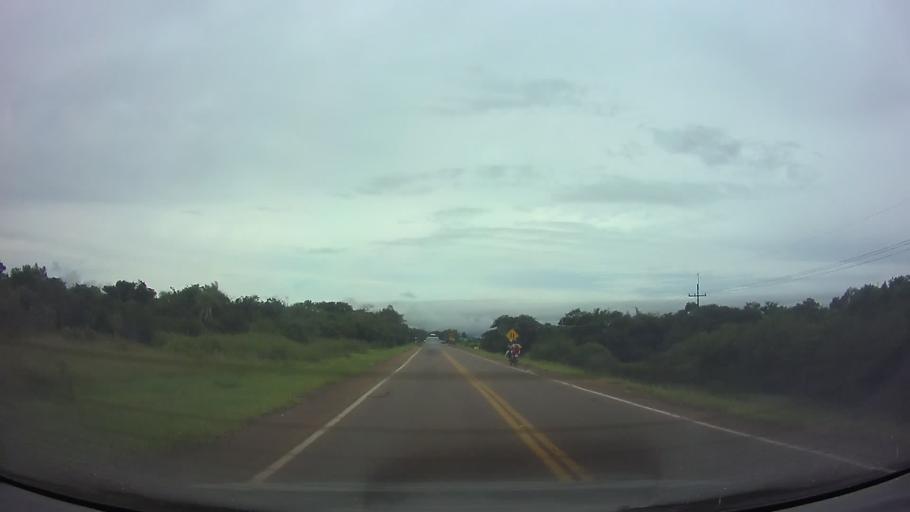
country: PY
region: Paraguari
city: Carapegua
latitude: -25.7273
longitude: -57.2054
